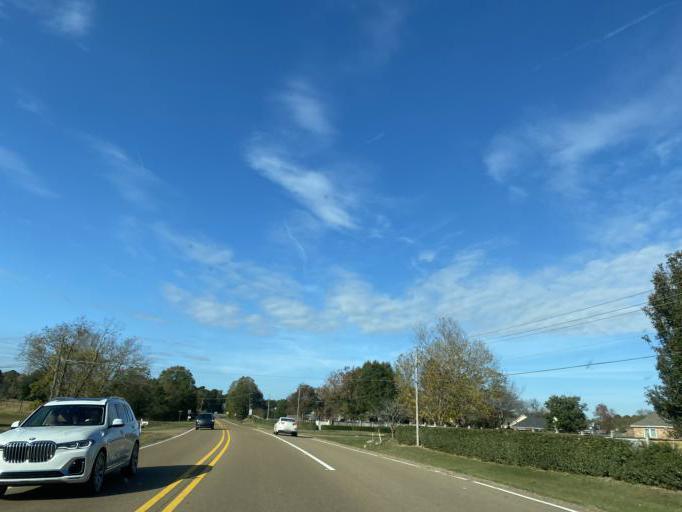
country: US
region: Mississippi
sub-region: Madison County
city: Madison
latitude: 32.4804
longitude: -90.1607
